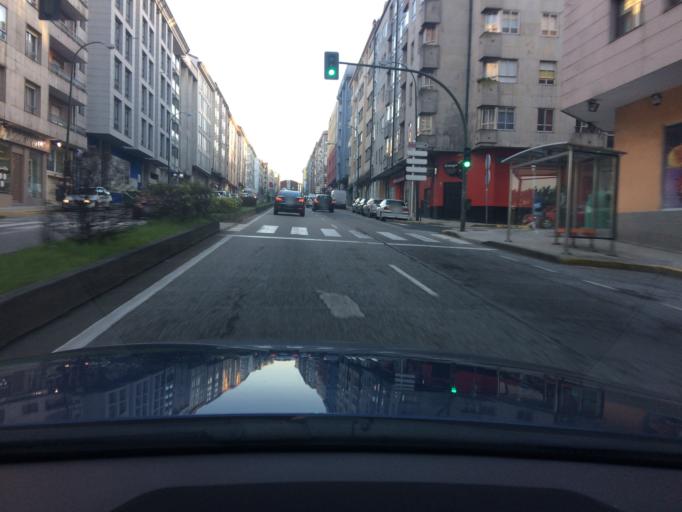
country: ES
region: Galicia
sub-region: Provincia da Coruna
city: Santiago de Compostela
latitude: 42.8475
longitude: -8.5747
